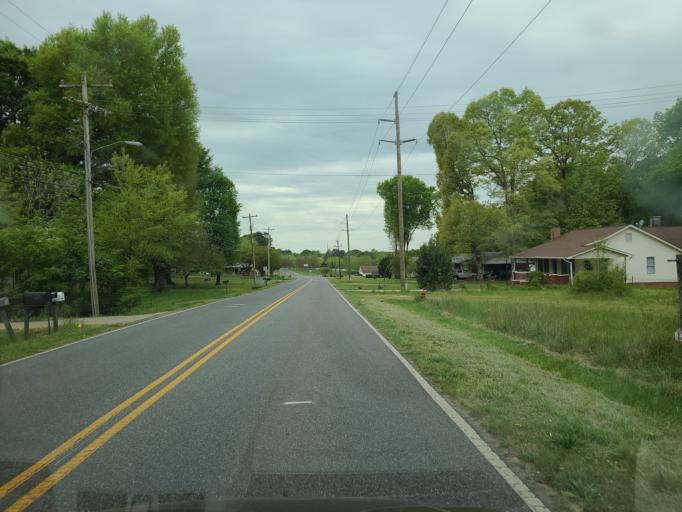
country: US
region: North Carolina
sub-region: Cleveland County
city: Shelby
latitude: 35.3054
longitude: -81.5027
